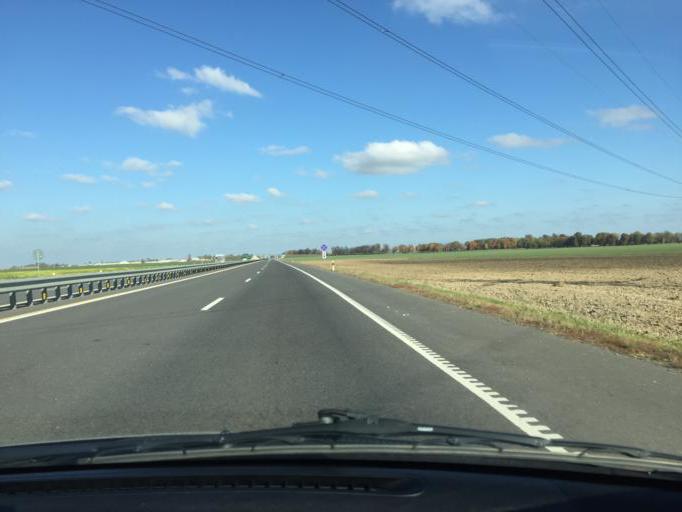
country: BY
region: Minsk
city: Slutsk
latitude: 53.0569
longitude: 27.5421
